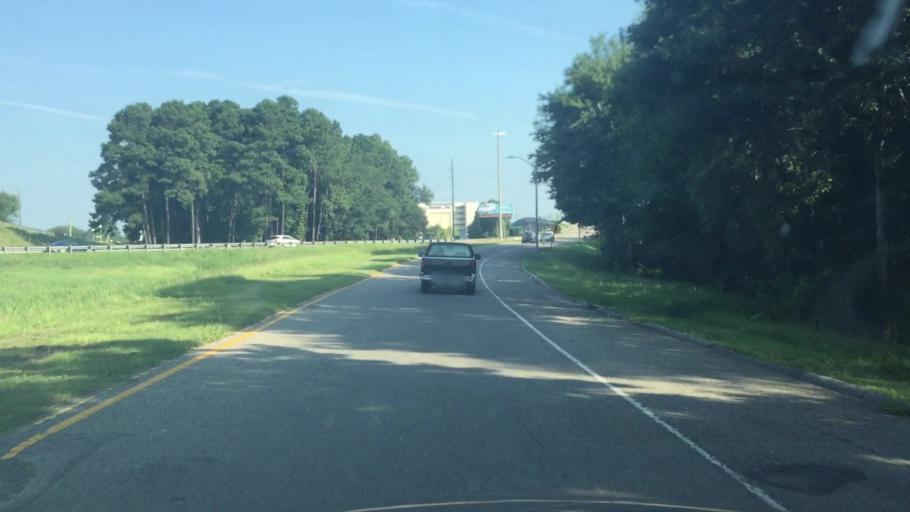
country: US
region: South Carolina
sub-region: Horry County
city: North Myrtle Beach
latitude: 33.8473
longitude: -78.6520
